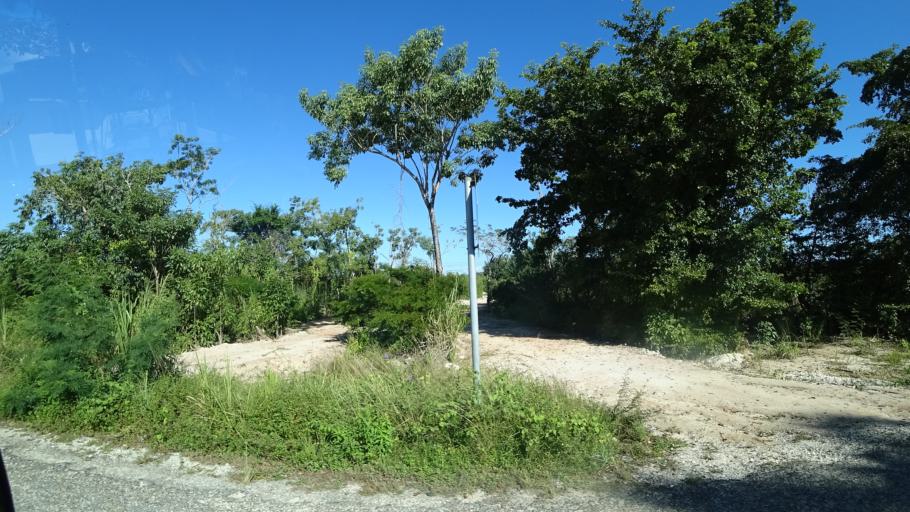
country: BZ
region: Belize
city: Belize City
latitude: 17.5452
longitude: -88.2824
